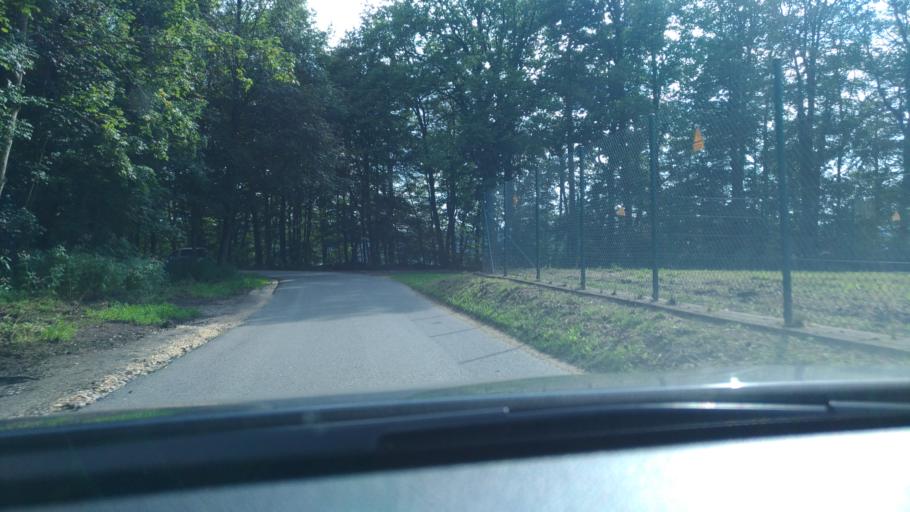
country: DE
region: Baden-Wuerttemberg
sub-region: Tuebingen Region
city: Sipplingen
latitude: 47.7924
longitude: 9.1232
